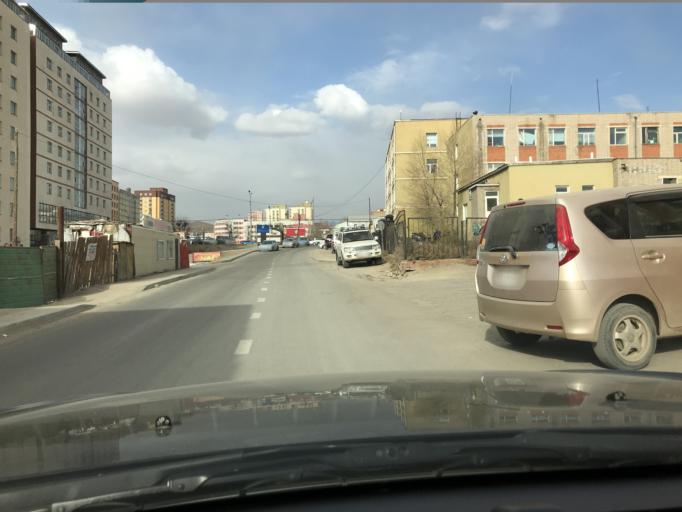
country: MN
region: Ulaanbaatar
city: Ulaanbaatar
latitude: 47.9151
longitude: 106.9641
